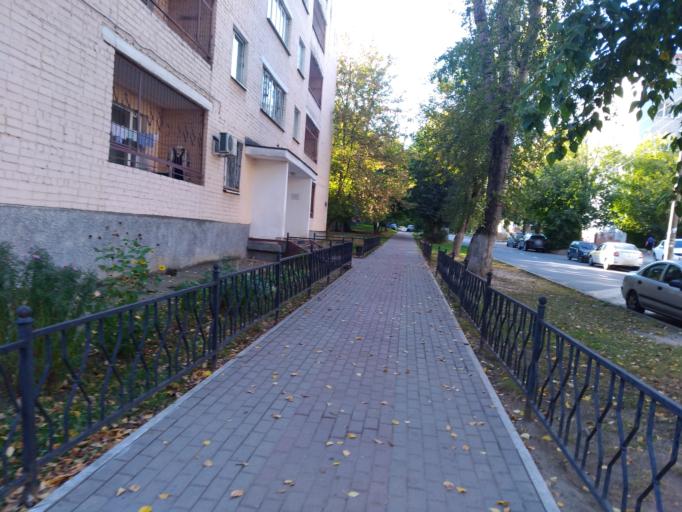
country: RU
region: Kaluga
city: Kaluga
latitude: 54.5178
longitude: 36.2717
